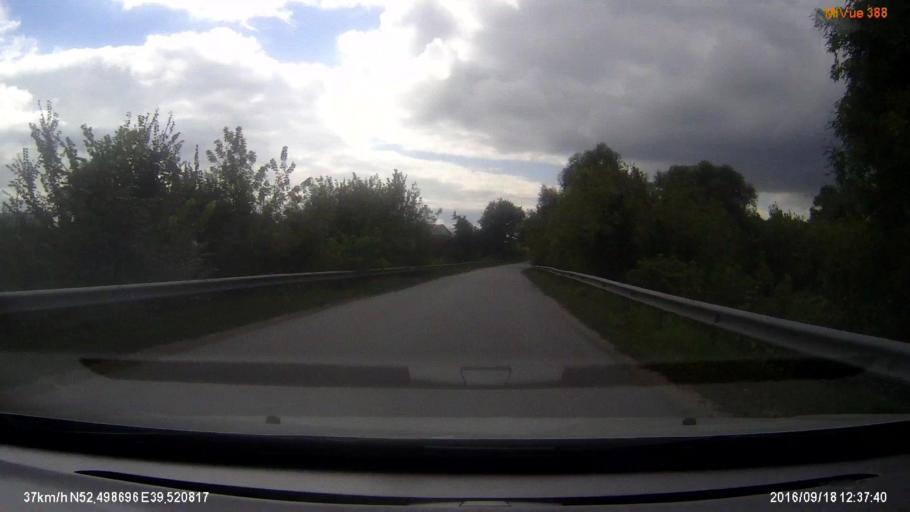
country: RU
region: Lipetsk
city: Syrskoye
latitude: 52.4984
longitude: 39.5206
